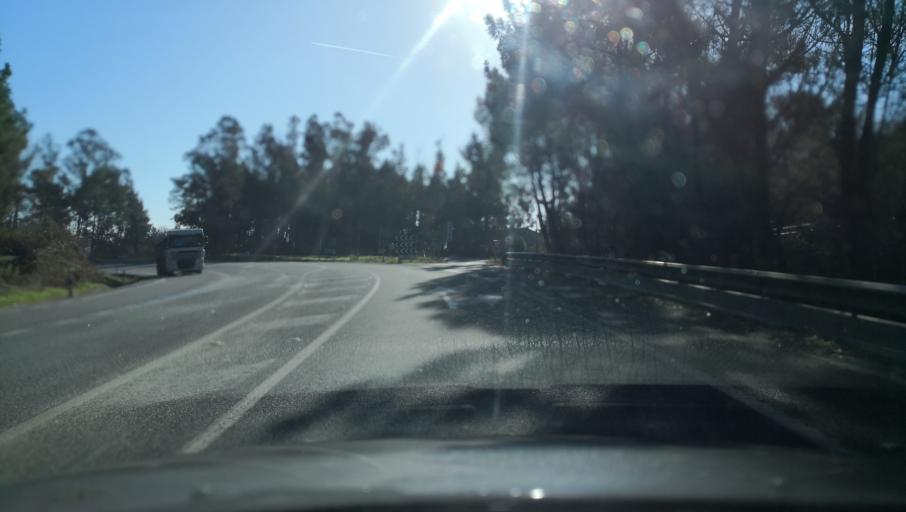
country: ES
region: Galicia
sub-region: Provincia da Coruna
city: Vedra
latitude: 42.7910
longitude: -8.4583
